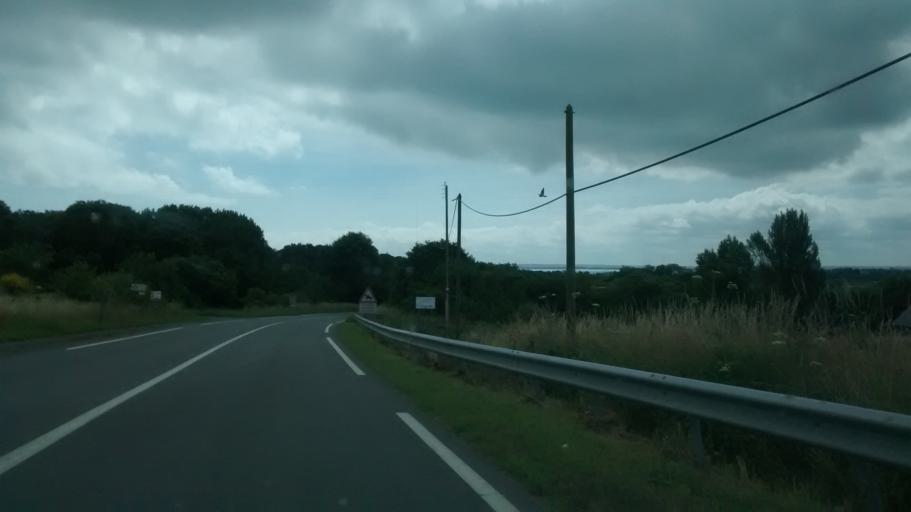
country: FR
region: Brittany
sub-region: Departement d'Ille-et-Vilaine
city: Saint-Meloir-des-Ondes
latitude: 48.6443
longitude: -1.8836
